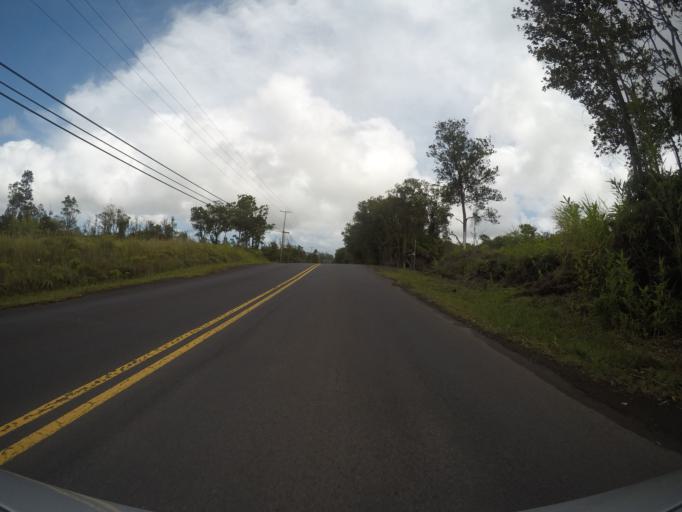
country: US
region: Hawaii
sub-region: Hawaii County
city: Fern Acres
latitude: 19.4810
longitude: -155.1445
